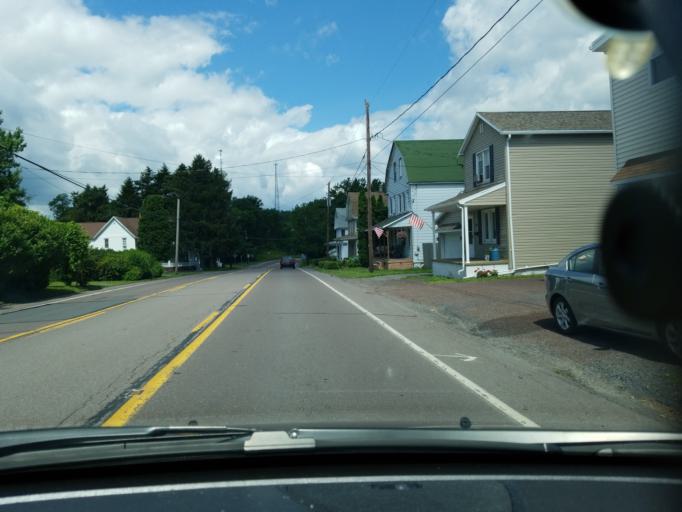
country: US
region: Pennsylvania
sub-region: Northumberland County
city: Kulpmont
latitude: 40.8176
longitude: -76.4632
